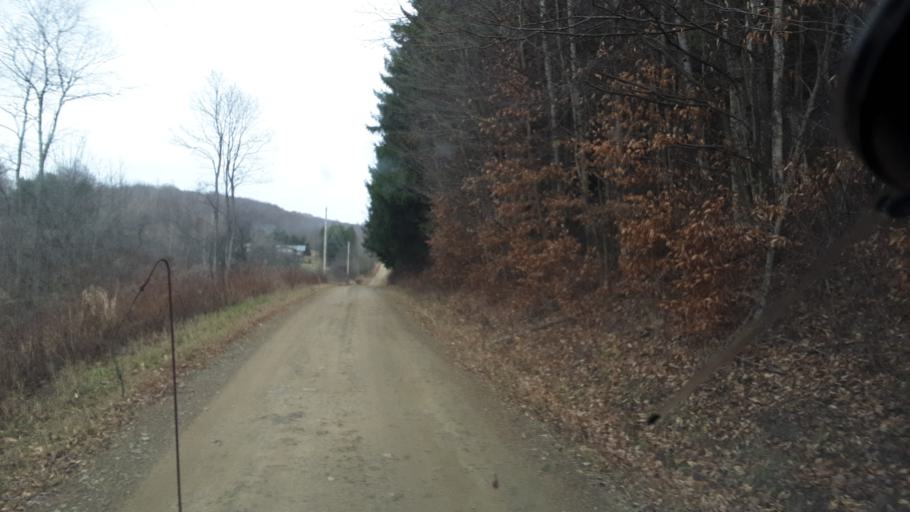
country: US
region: Pennsylvania
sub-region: Tioga County
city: Westfield
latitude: 41.9104
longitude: -77.7079
